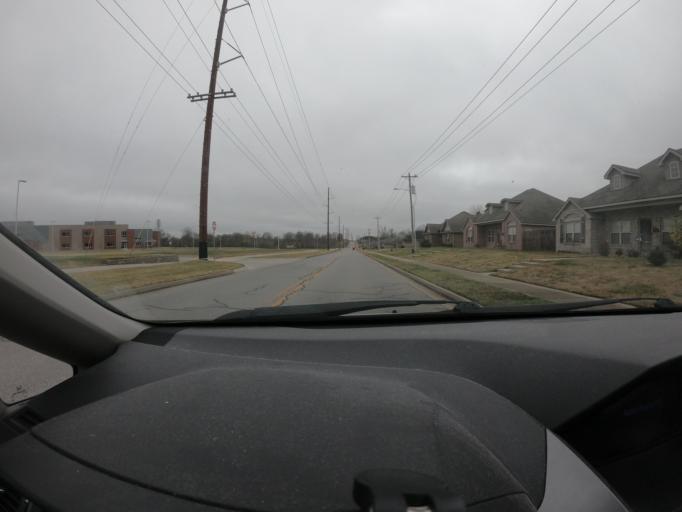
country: US
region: Arkansas
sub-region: Benton County
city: Centerton
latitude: 36.3426
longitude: -94.2448
